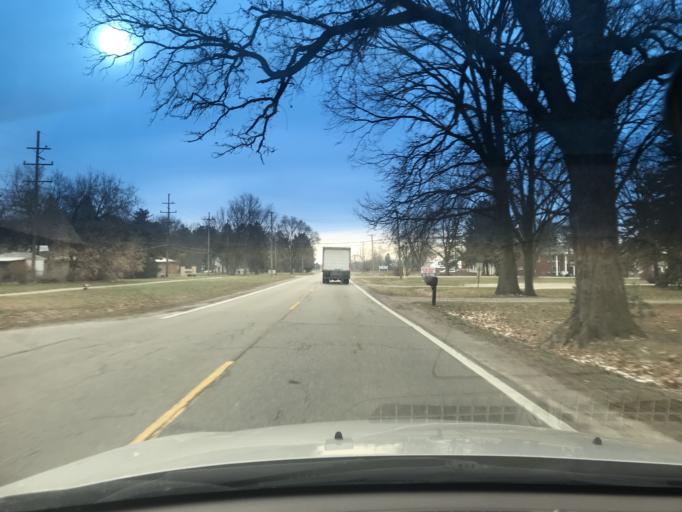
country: US
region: Michigan
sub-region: Macomb County
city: Shelby
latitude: 42.6744
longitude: -83.0537
